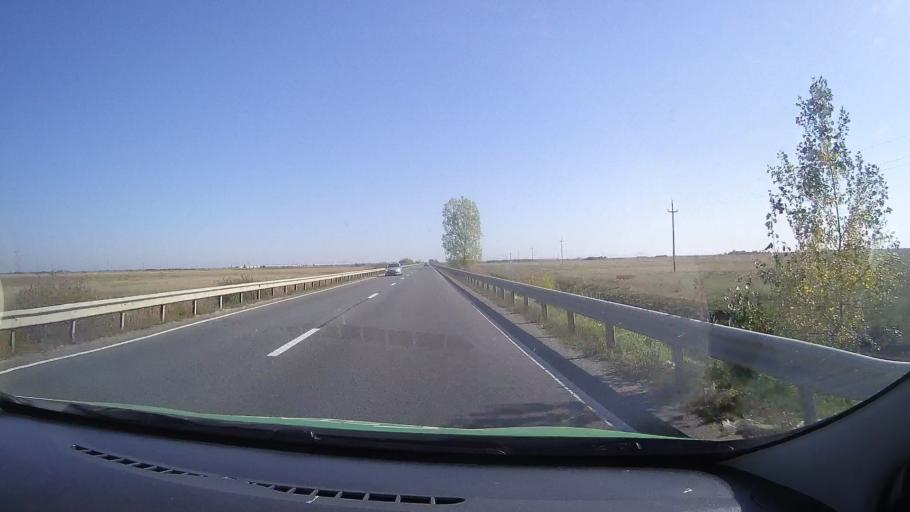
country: RO
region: Satu Mare
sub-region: Comuna Capleni
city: Capleni
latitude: 47.6851
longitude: 22.5300
